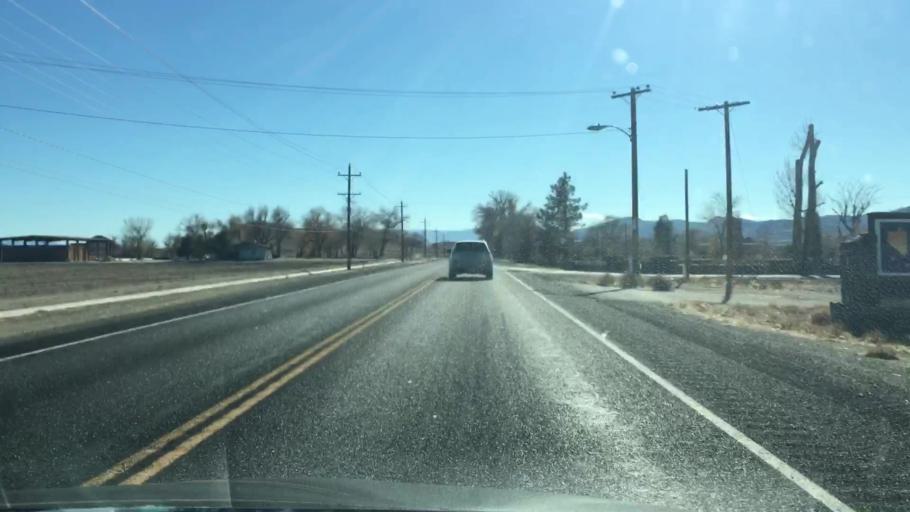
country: US
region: Nevada
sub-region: Lyon County
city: Yerington
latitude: 39.0345
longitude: -119.1816
